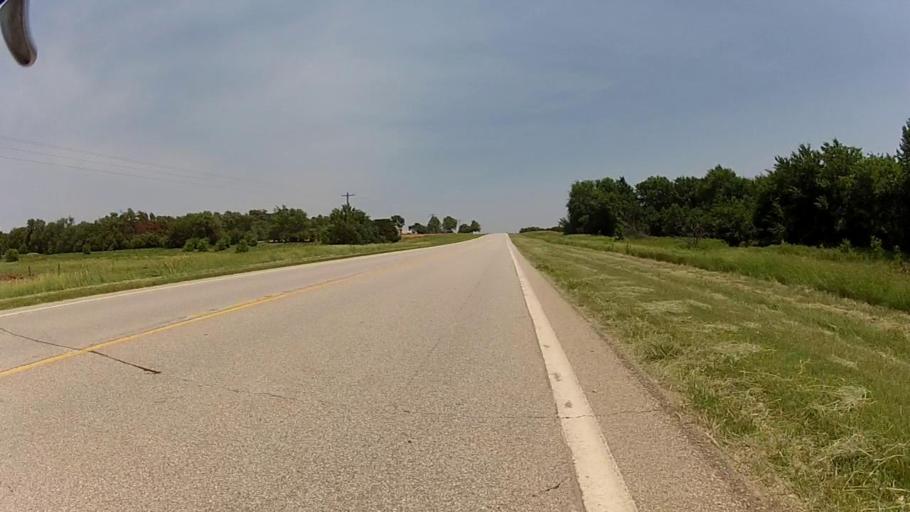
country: US
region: Kansas
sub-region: Cowley County
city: Arkansas City
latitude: 37.0568
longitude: -97.2346
